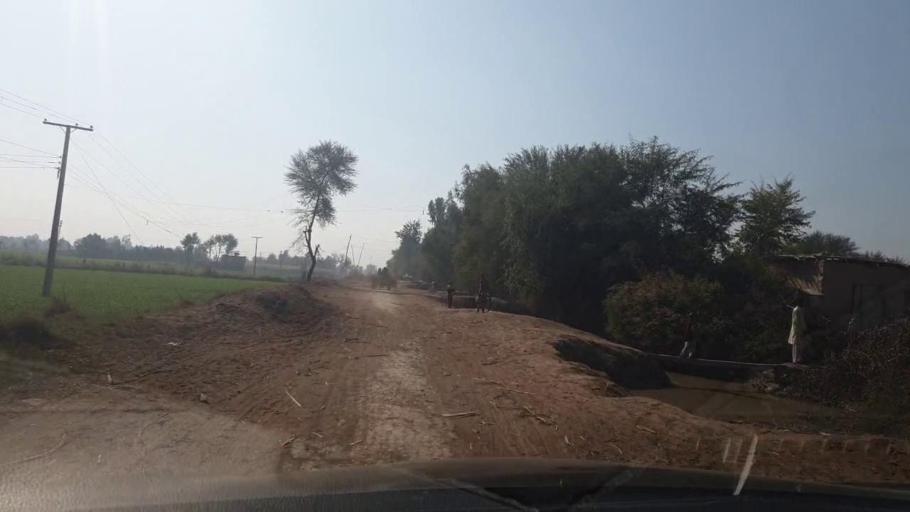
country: PK
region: Sindh
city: Ubauro
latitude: 28.1543
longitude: 69.6949
